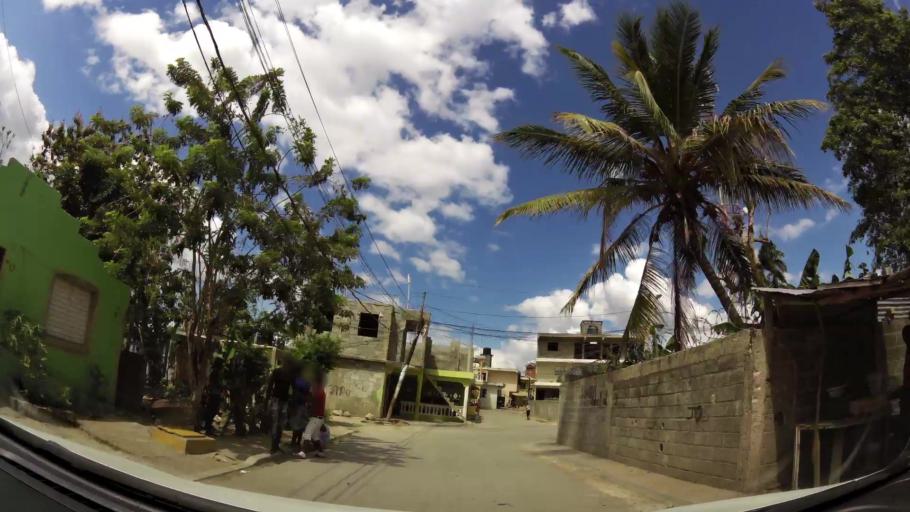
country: DO
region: Nacional
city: Ensanche Luperon
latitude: 18.5315
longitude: -69.9125
